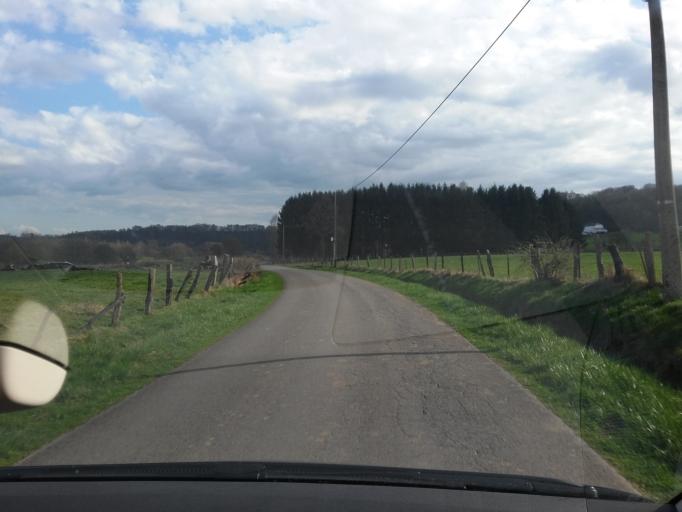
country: BE
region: Wallonia
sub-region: Province du Luxembourg
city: Florenville
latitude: 49.7173
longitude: 5.2585
